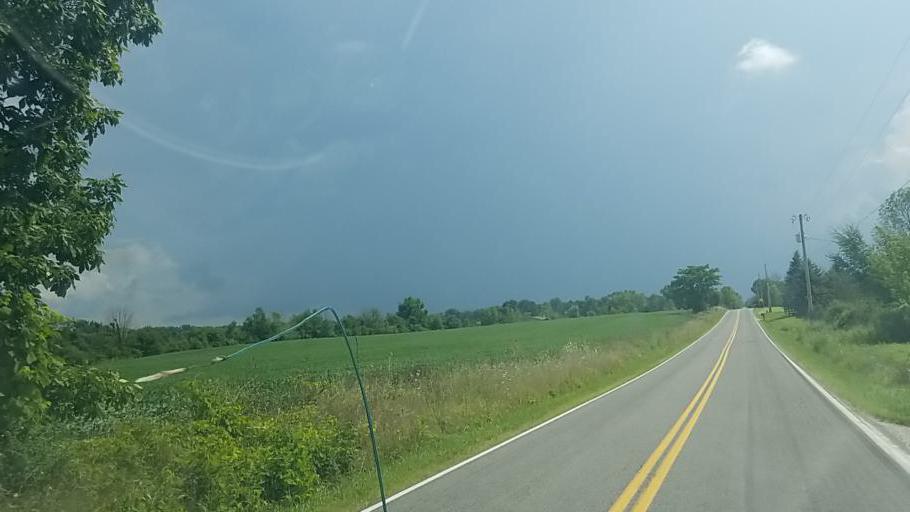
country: US
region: Ohio
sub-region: Medina County
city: Lodi
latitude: 41.0896
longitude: -82.0042
